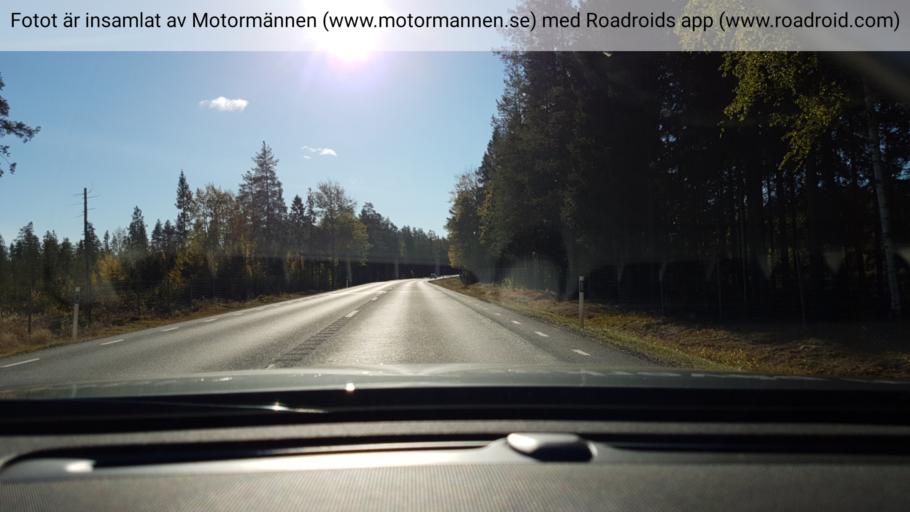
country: SE
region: Vaesterbotten
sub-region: Skelleftea Kommun
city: Burea
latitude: 64.5876
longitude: 21.2167
